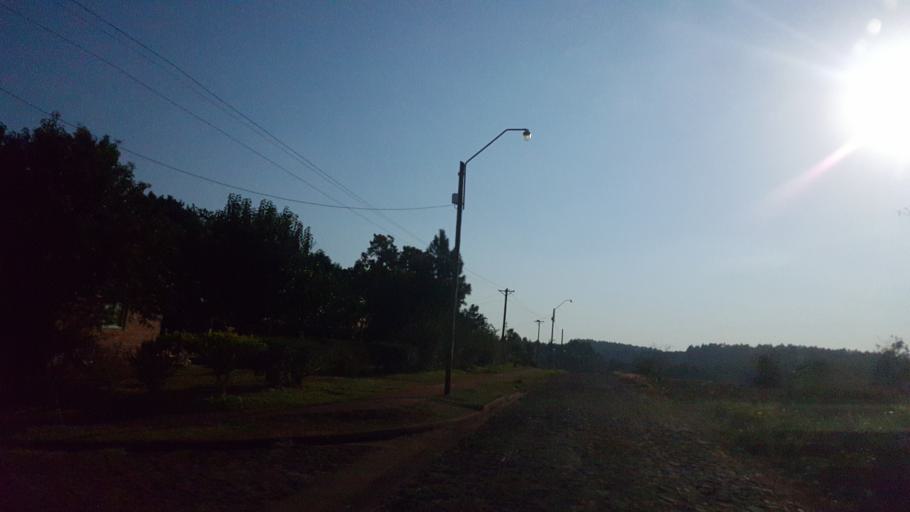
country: AR
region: Misiones
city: Capiovi
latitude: -26.8926
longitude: -55.0712
